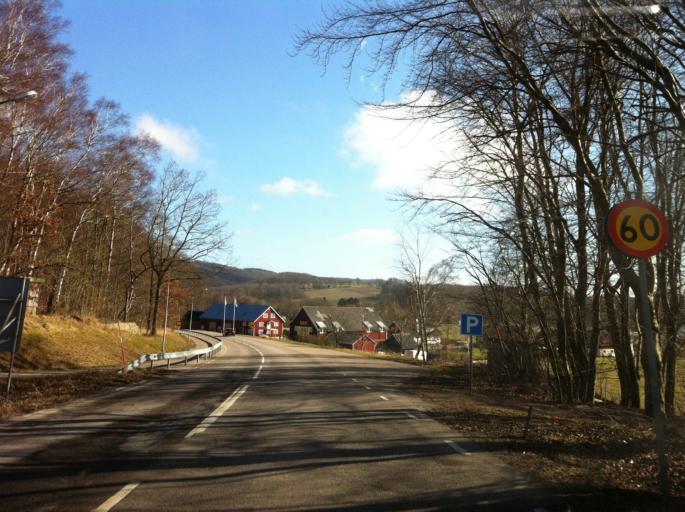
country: SE
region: Skane
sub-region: Bastads Kommun
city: Forslov
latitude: 56.3651
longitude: 12.8070
